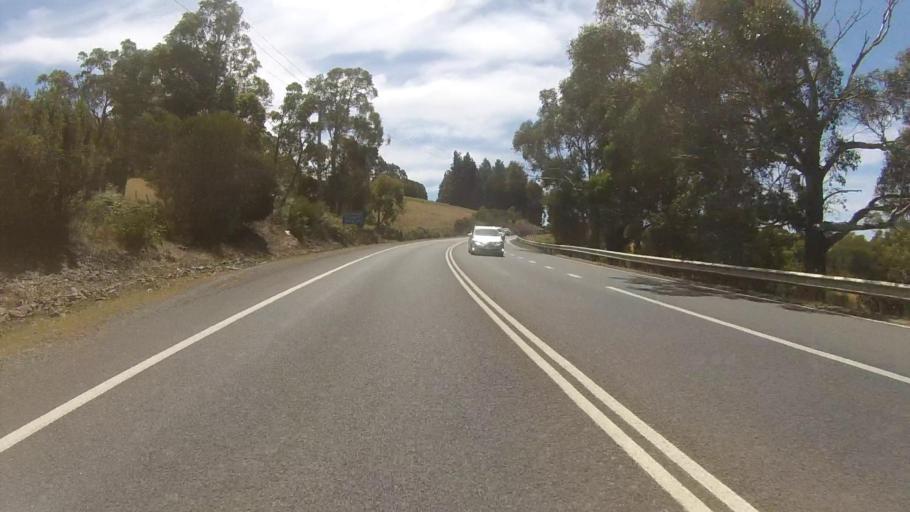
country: AU
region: Tasmania
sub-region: Kingborough
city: Margate
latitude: -43.0065
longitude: 147.2727
